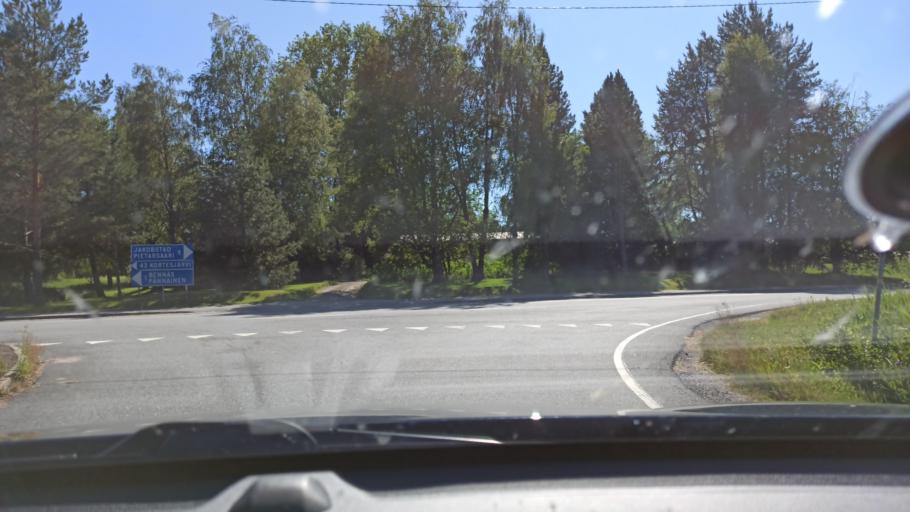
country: FI
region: Ostrobothnia
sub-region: Jakobstadsregionen
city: Bennaes
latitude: 63.6069
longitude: 22.7843
